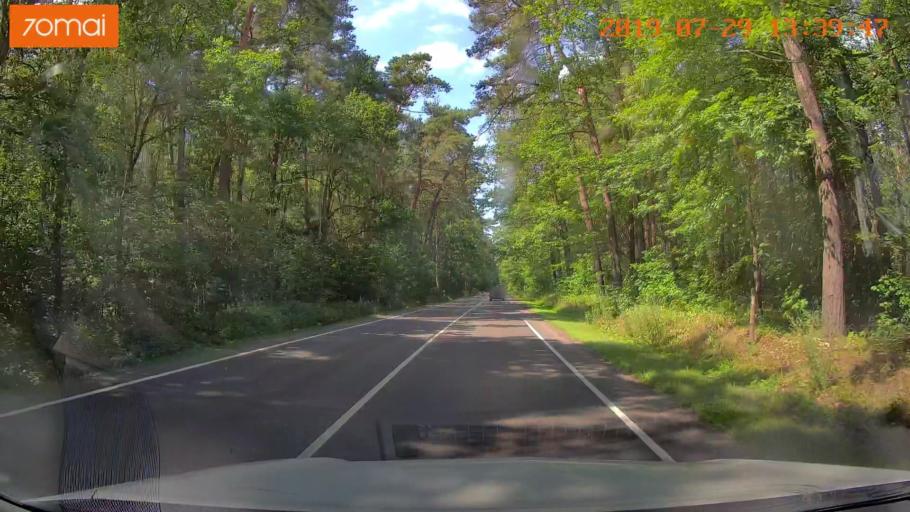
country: RU
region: Kaliningrad
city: Svetlyy
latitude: 54.7248
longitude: 20.1474
